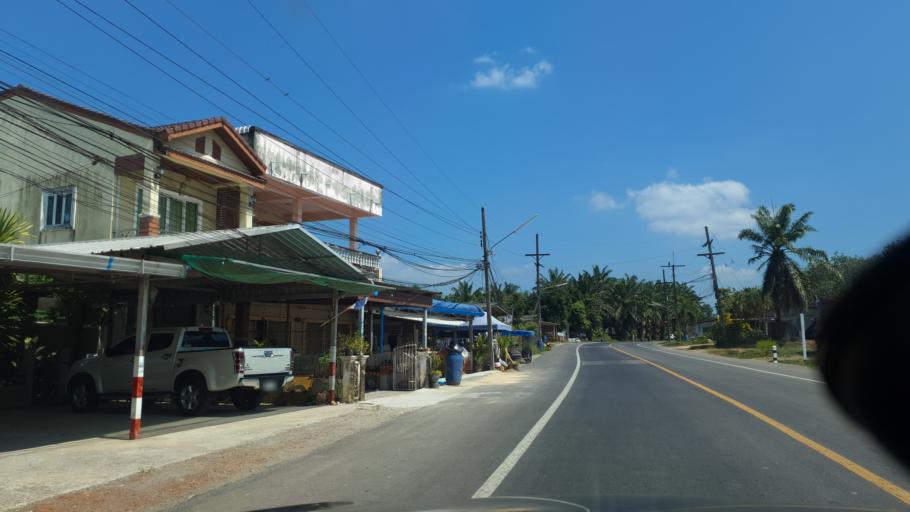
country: TH
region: Krabi
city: Khlong Thom
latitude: 7.9388
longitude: 99.1483
